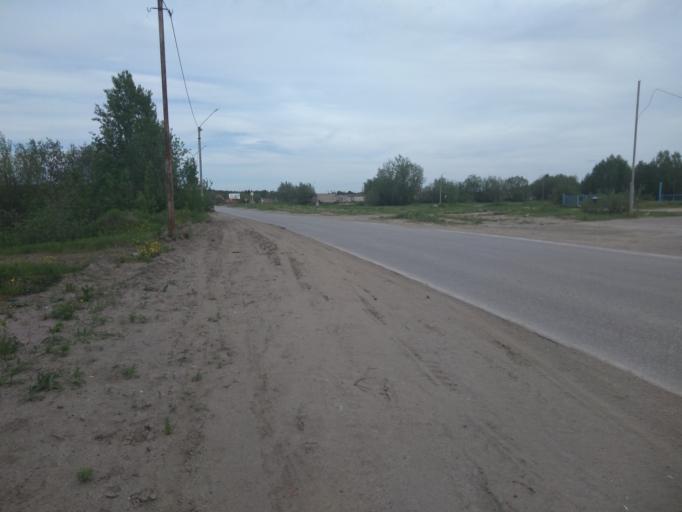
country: RU
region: Komi Republic
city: Pechora
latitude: 65.1435
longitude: 57.2451
